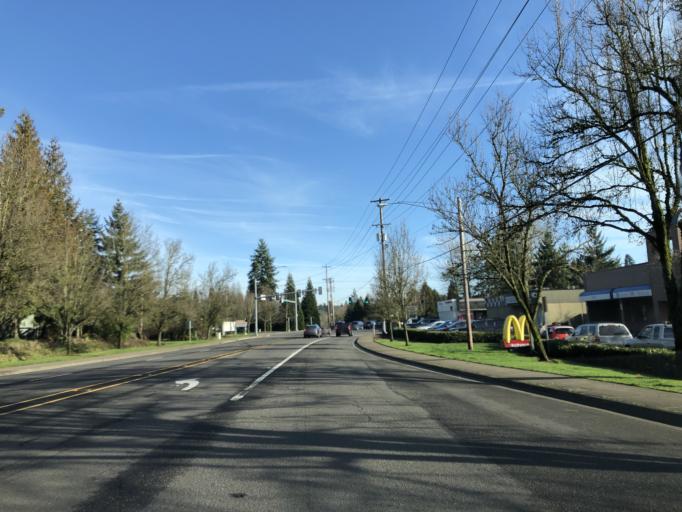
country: US
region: Oregon
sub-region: Washington County
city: Tualatin
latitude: 45.3827
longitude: -122.7464
